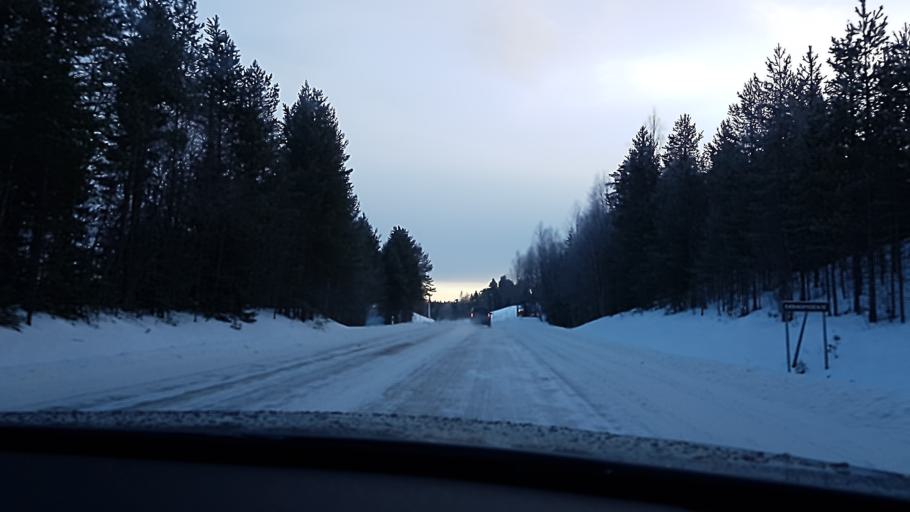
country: SE
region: Jaemtland
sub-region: Bergs Kommun
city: Hoverberg
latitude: 62.4636
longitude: 14.5287
